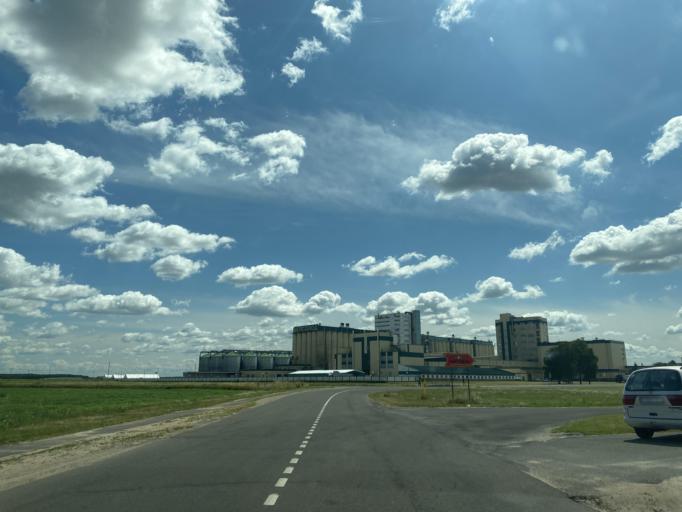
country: BY
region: Brest
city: Ivanava
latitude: 52.1397
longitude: 25.5520
